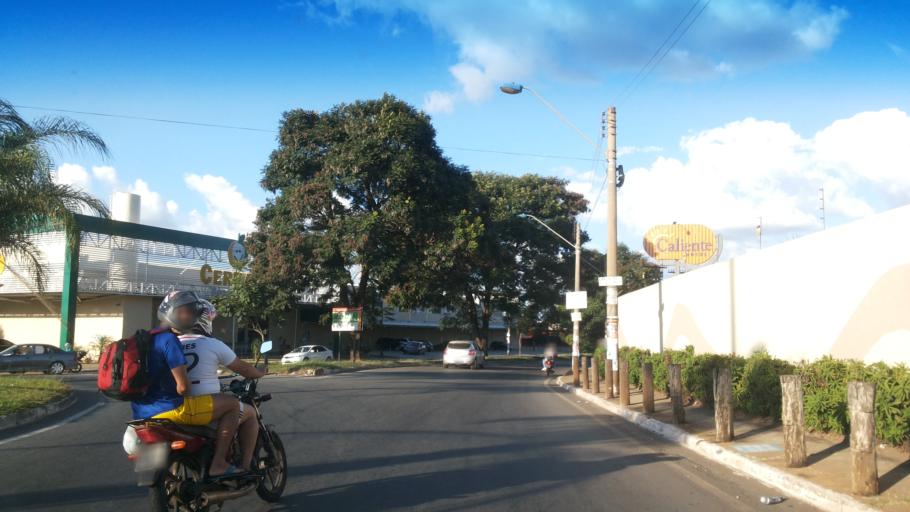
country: BR
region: Goias
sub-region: Goiania
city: Goiania
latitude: -16.7495
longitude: -49.3321
